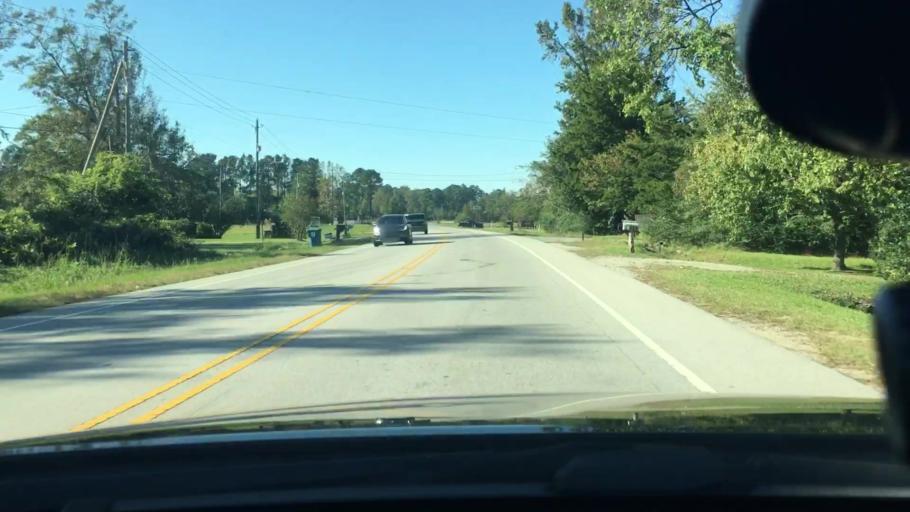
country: US
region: North Carolina
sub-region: Craven County
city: Trent Woods
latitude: 35.1577
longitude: -77.1146
